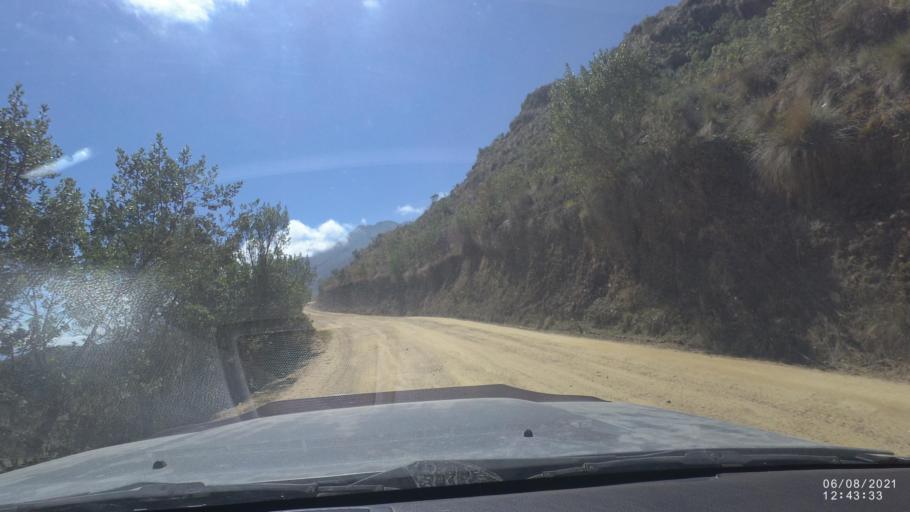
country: BO
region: Cochabamba
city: Colchani
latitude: -16.7727
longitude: -66.6673
